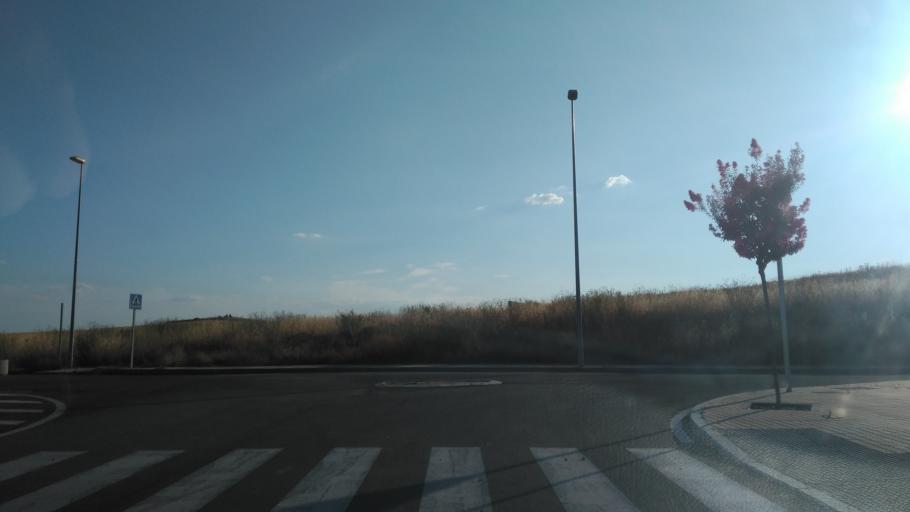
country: ES
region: Castille and Leon
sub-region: Provincia de Salamanca
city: Carbajosa de la Sagrada
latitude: 40.9297
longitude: -5.6508
